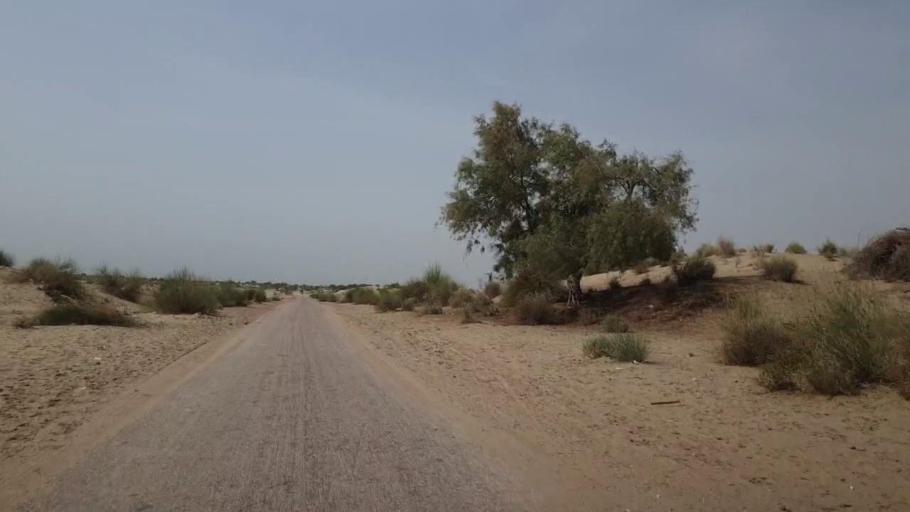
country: PK
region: Sindh
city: Bandhi
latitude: 26.5400
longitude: 68.3865
